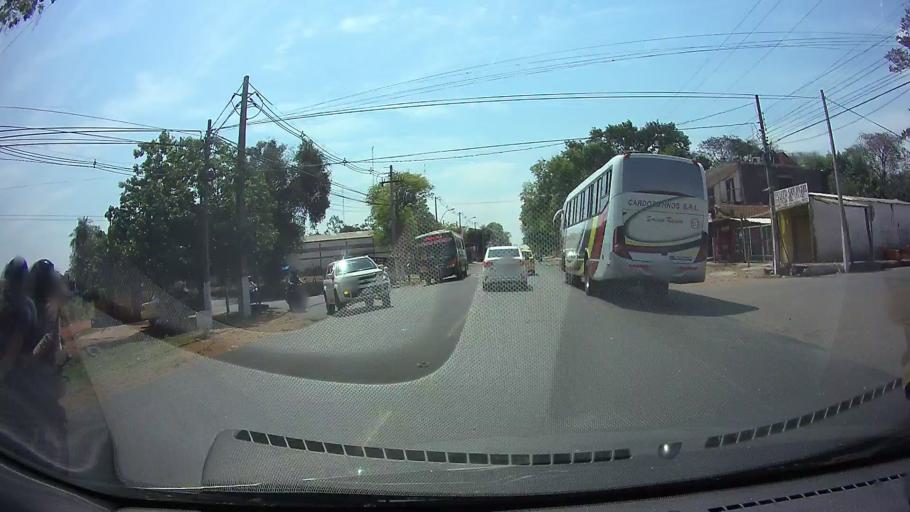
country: PY
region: Central
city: Capiata
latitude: -25.3844
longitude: -57.4726
